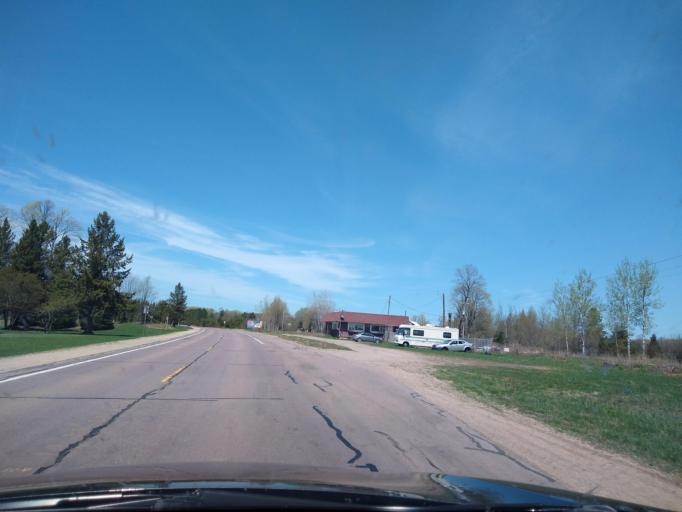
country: US
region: Michigan
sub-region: Marquette County
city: K. I. Sawyer Air Force Base
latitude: 46.2522
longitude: -87.0840
